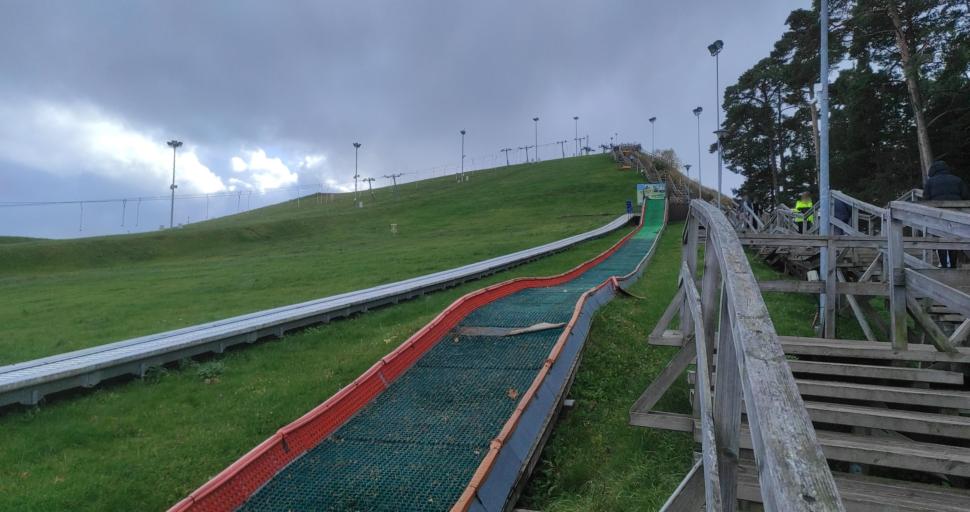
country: LV
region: Ventspils
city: Ventspils
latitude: 57.3747
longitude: 21.5476
